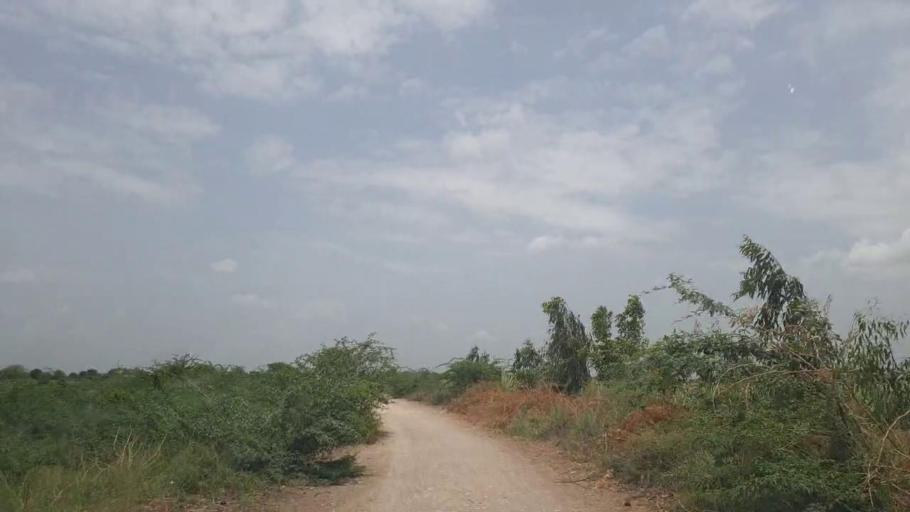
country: PK
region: Sindh
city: Naukot
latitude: 24.9306
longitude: 69.1995
